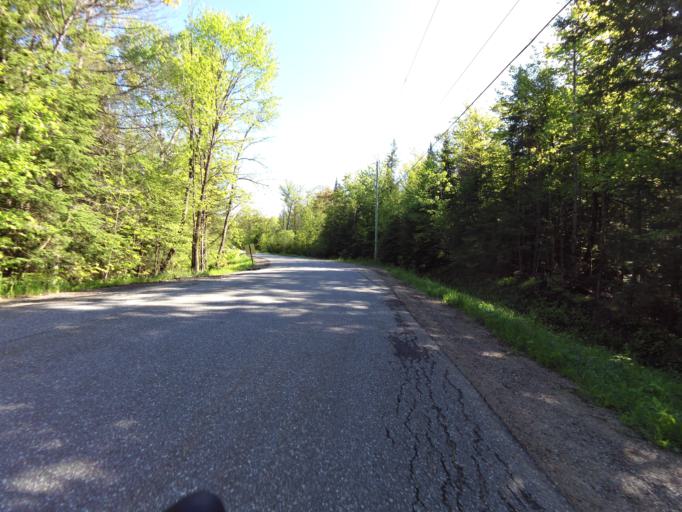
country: CA
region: Quebec
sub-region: Outaouais
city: Wakefield
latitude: 45.6121
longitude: -75.8817
